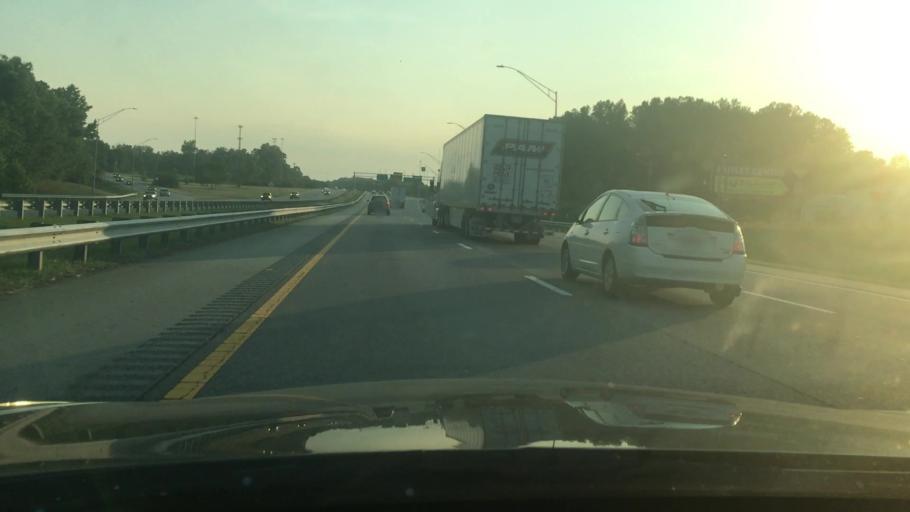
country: US
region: North Carolina
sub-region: Guilford County
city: Greensboro
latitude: 36.0533
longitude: -79.7287
